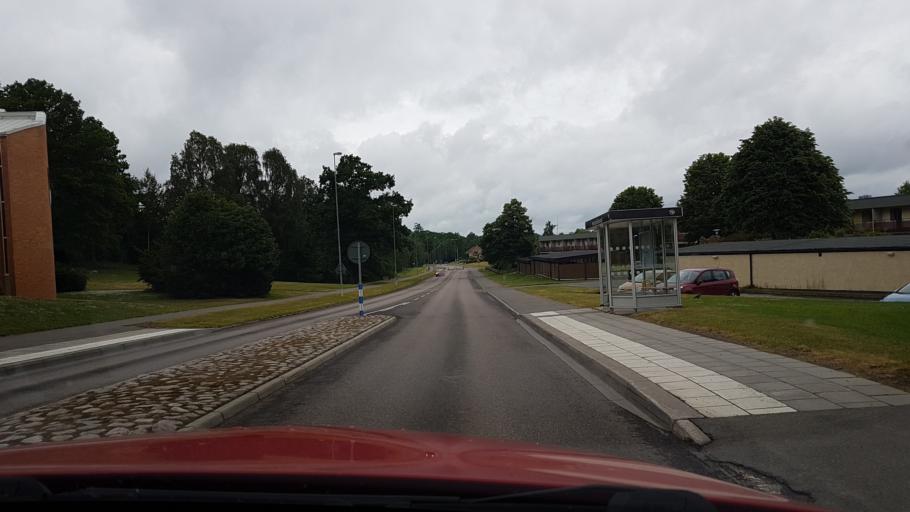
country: SE
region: Vaestra Goetaland
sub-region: Skovde Kommun
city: Skultorp
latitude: 58.3704
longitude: 13.8292
